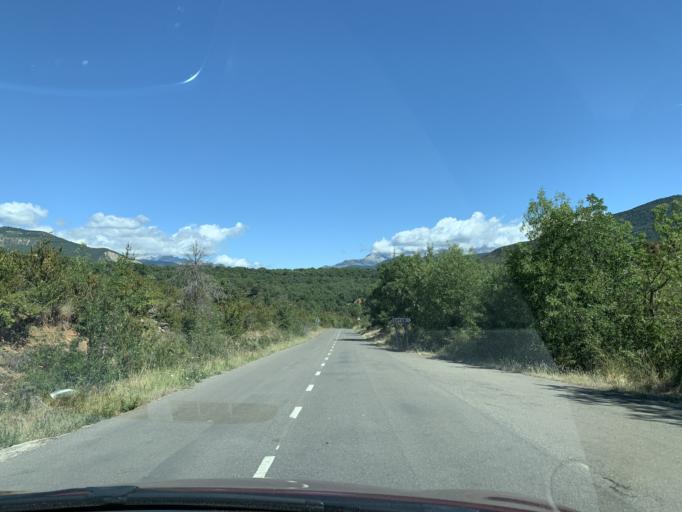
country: ES
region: Aragon
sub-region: Provincia de Huesca
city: Sabinanigo
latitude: 42.5317
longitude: -0.3236
